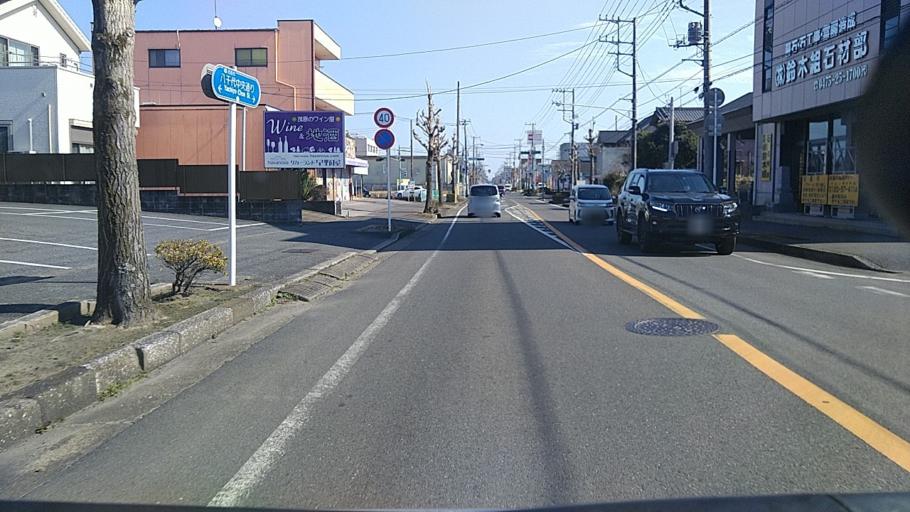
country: JP
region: Chiba
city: Mobara
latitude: 35.4239
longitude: 140.2922
